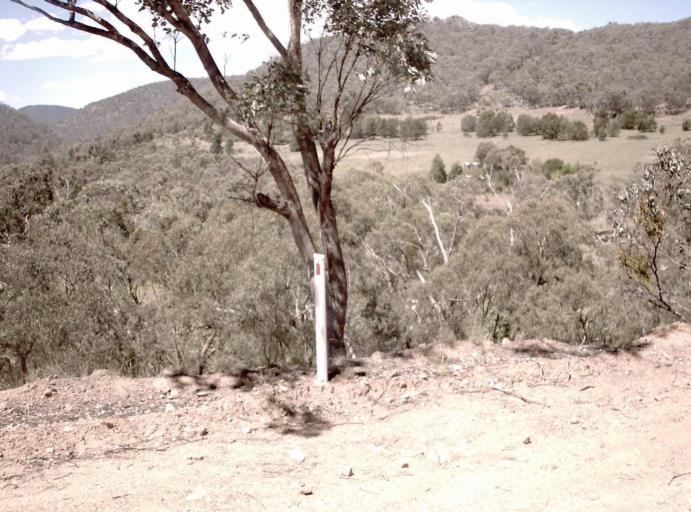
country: AU
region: New South Wales
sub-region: Snowy River
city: Jindabyne
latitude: -37.0669
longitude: 148.5121
